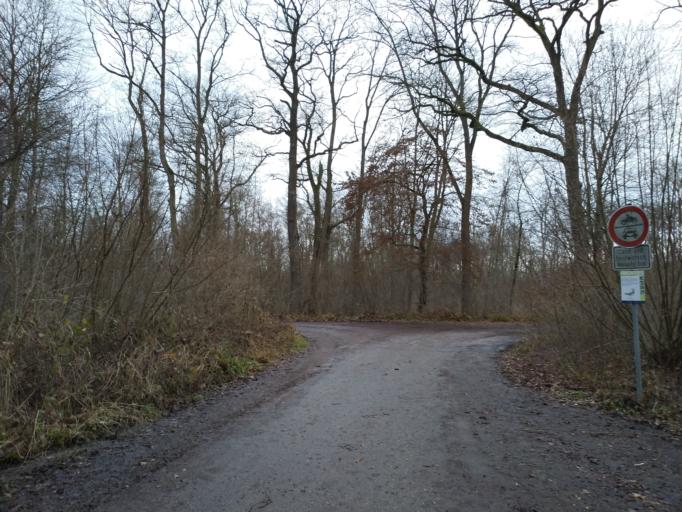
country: DE
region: Bavaria
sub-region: Swabia
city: Bachingen an der Brenz
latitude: 48.4975
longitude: 10.3053
